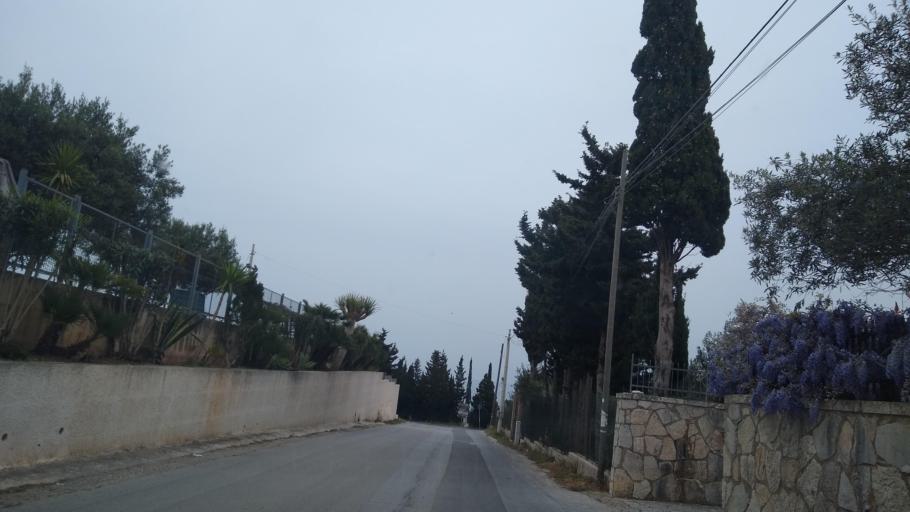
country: IT
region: Sicily
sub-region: Trapani
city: Castellammare del Golfo
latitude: 38.0189
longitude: 12.8979
